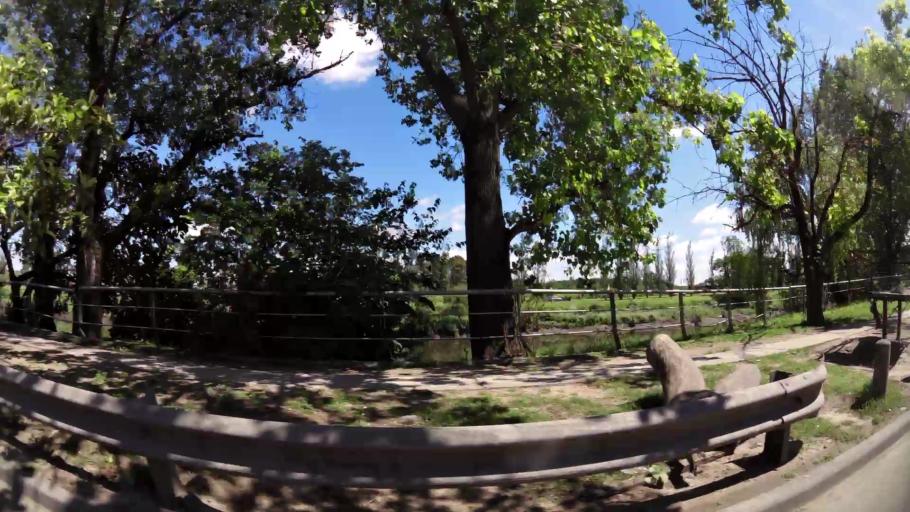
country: AR
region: Buenos Aires F.D.
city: Villa Lugano
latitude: -34.6727
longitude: -58.4328
